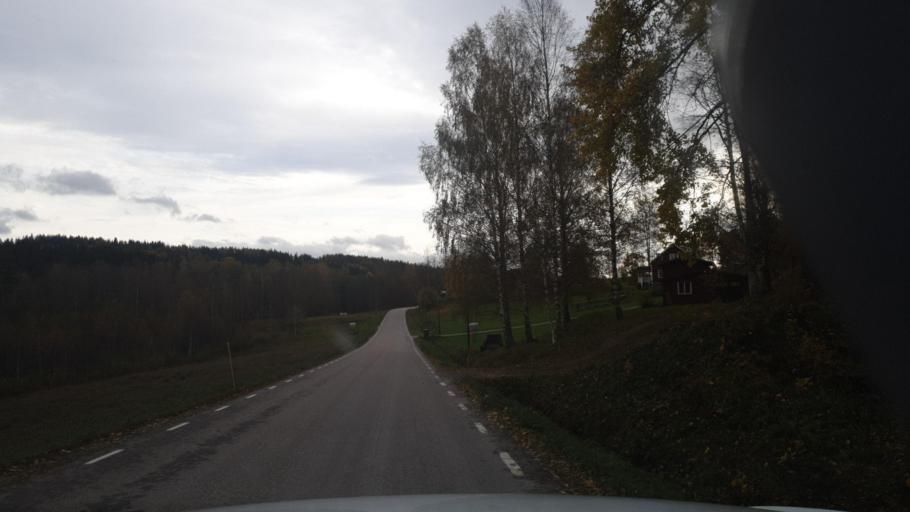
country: SE
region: Vaermland
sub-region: Arvika Kommun
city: Arvika
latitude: 59.7808
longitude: 12.7730
